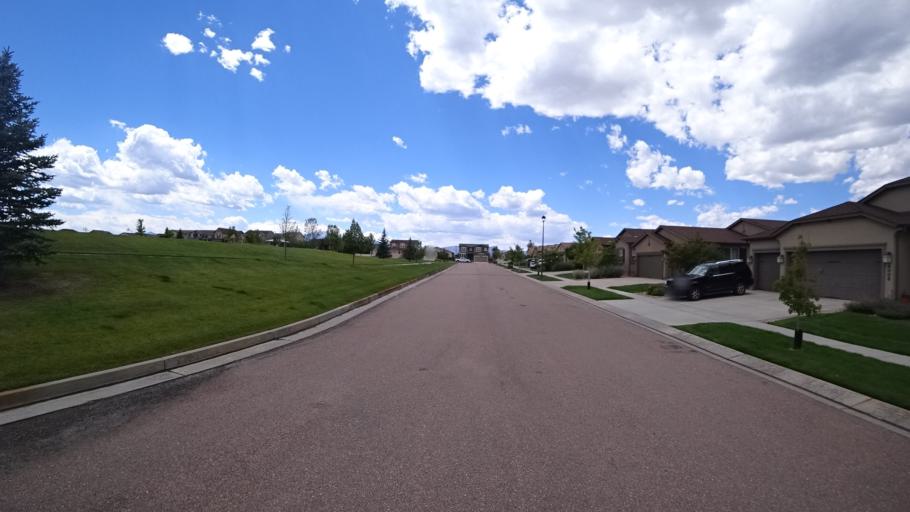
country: US
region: Colorado
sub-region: El Paso County
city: Black Forest
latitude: 38.9483
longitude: -104.7105
